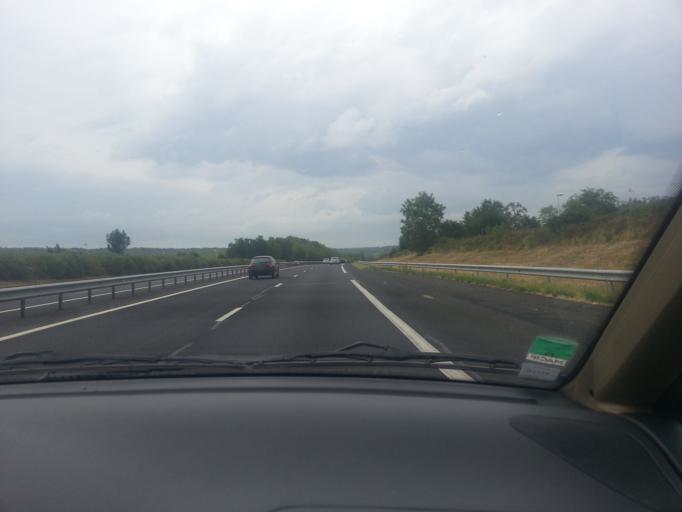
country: FR
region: Auvergne
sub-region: Departement du Puy-de-Dome
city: Le Breuil-sur-Couze
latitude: 45.4704
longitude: 3.2487
